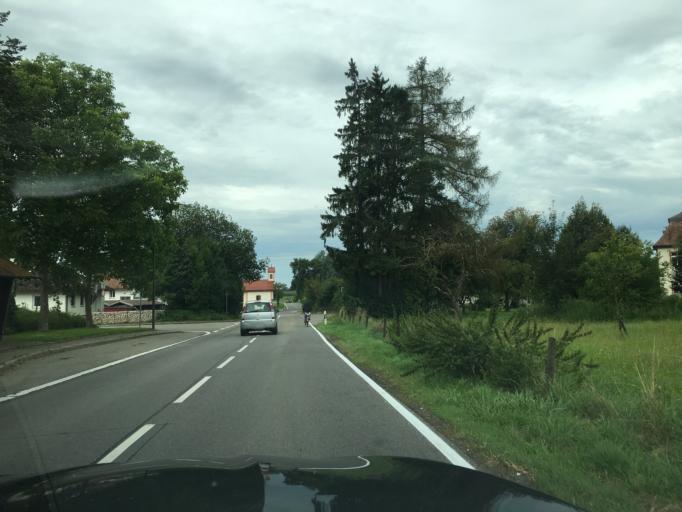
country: DE
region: Baden-Wuerttemberg
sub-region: Tuebingen Region
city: Rot
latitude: 47.8761
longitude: 9.1109
